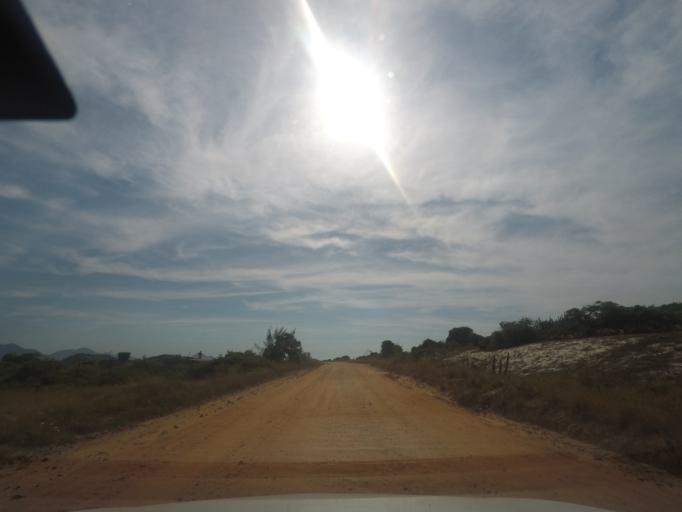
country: BR
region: Rio de Janeiro
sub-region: Marica
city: Marica
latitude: -22.9604
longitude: -42.8425
